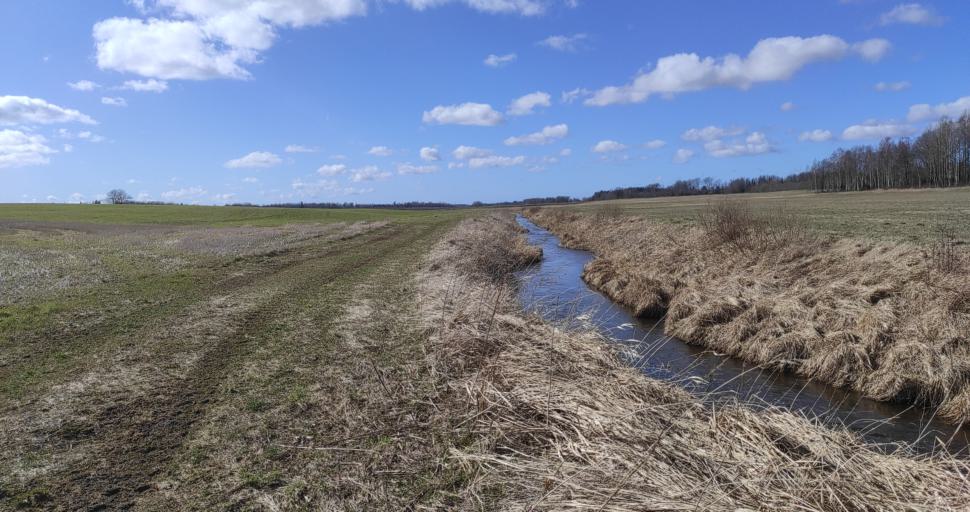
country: LV
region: Aizpute
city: Aizpute
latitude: 56.8462
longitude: 21.7499
